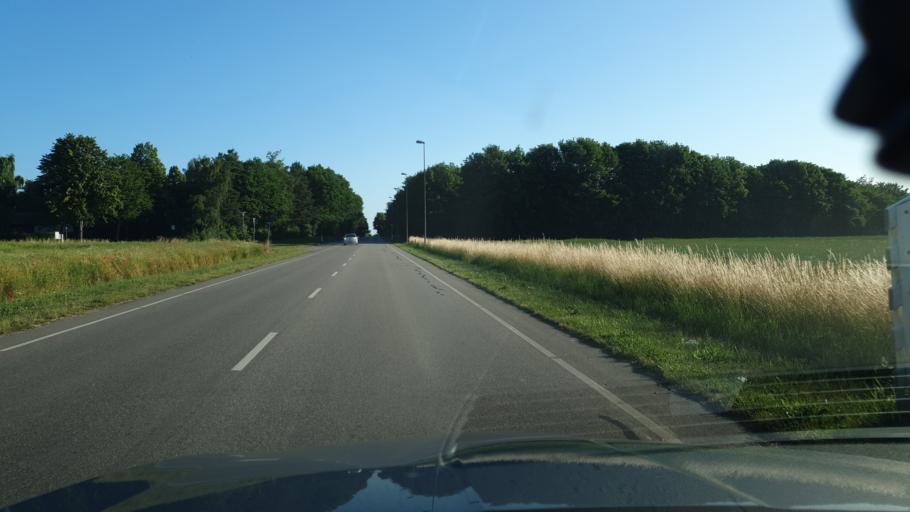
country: DK
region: Zealand
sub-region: Soro Kommune
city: Frederiksberg
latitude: 55.4059
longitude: 11.5640
